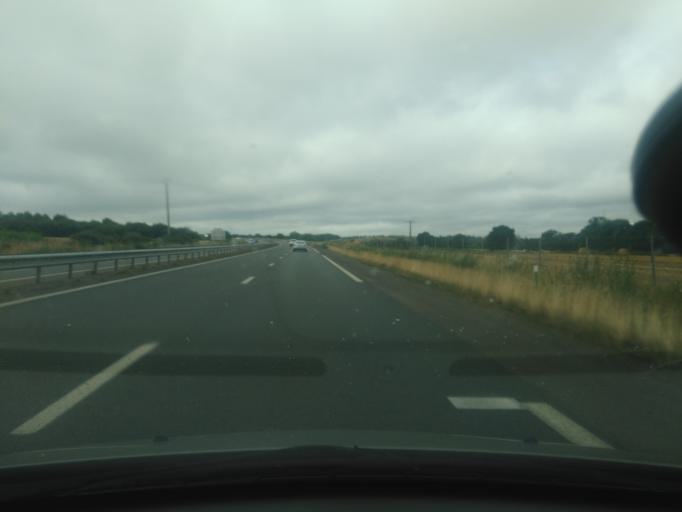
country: FR
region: Brittany
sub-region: Departement des Cotes-d'Armor
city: Pledeliac
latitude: 48.4126
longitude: -2.3961
